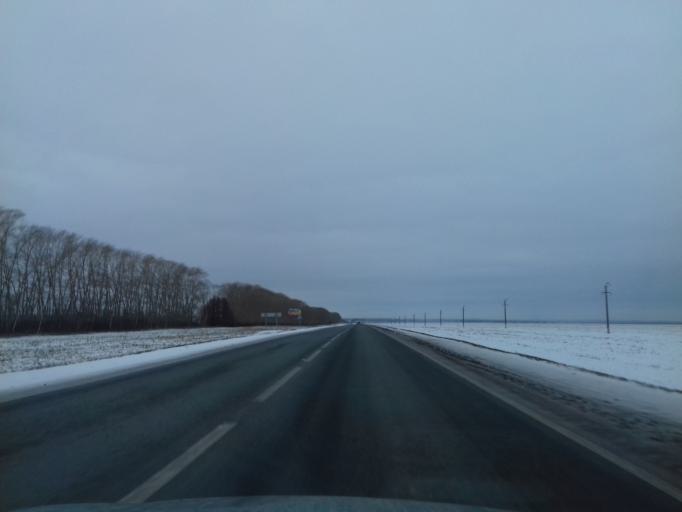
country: RU
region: Bashkortostan
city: Karmaskaly
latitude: 54.4090
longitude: 56.0712
